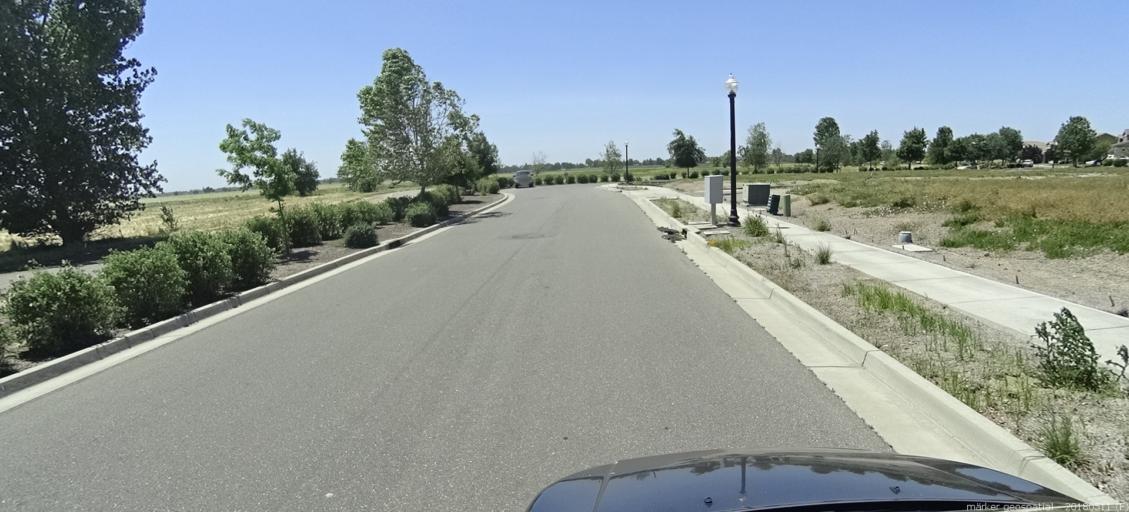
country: US
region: California
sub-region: Yolo County
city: West Sacramento
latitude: 38.6438
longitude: -121.5466
